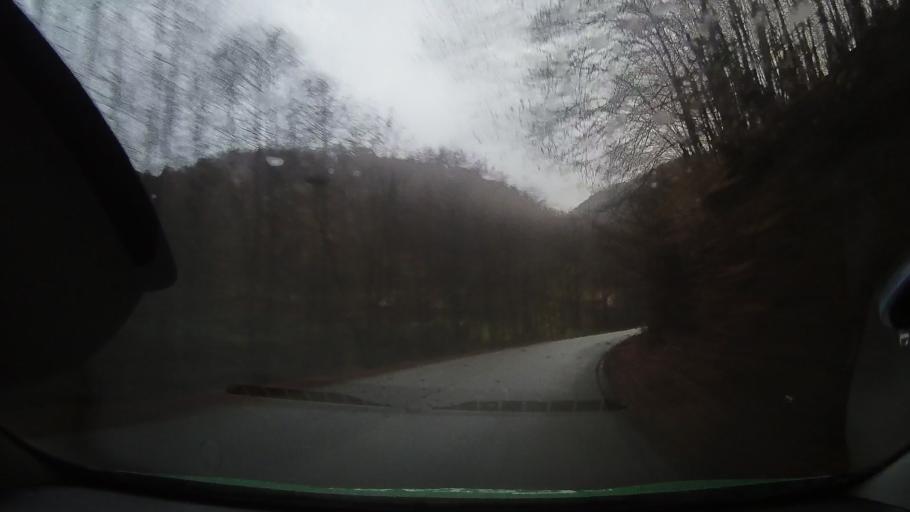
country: RO
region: Hunedoara
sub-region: Comuna Ribita
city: Ribita
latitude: 46.2816
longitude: 22.7356
